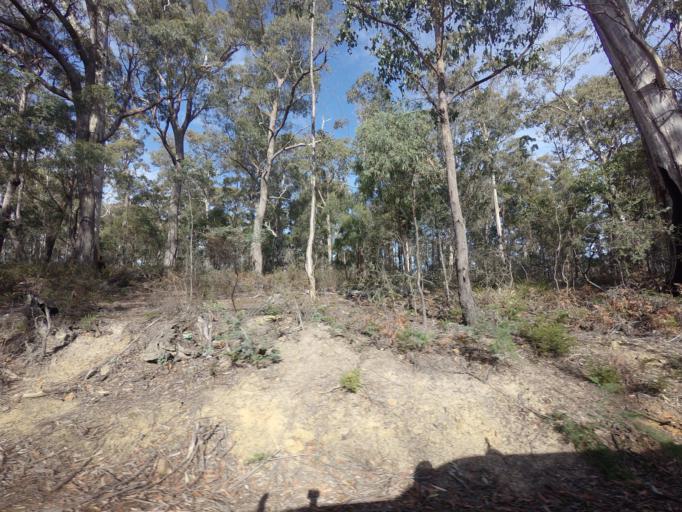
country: AU
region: Tasmania
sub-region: Sorell
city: Sorell
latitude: -42.5243
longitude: 147.4707
